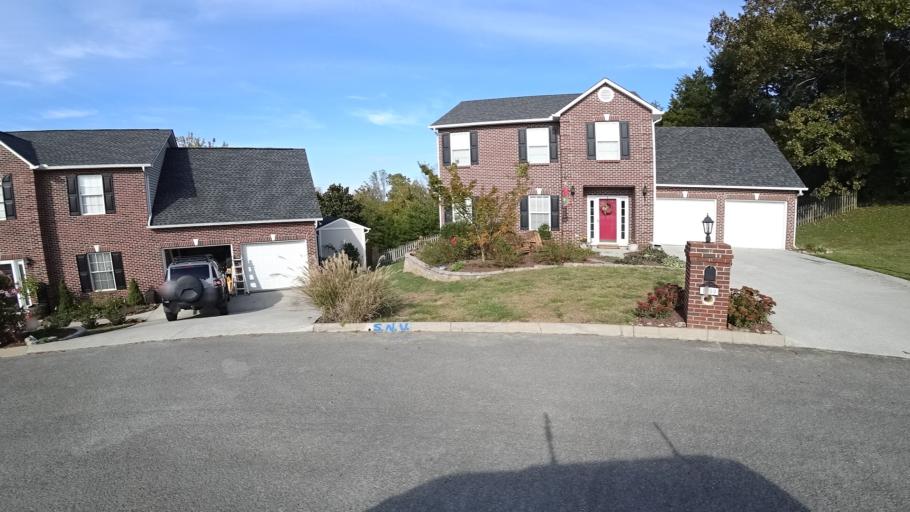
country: US
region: Tennessee
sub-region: Knox County
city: Farragut
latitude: 35.9158
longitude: -84.1692
